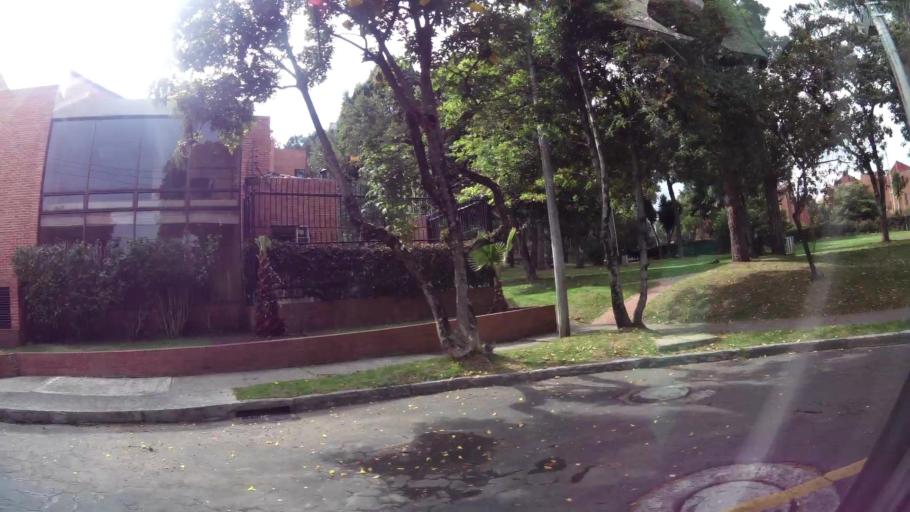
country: CO
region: Bogota D.C.
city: Barrio San Luis
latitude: 4.7184
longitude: -74.0288
